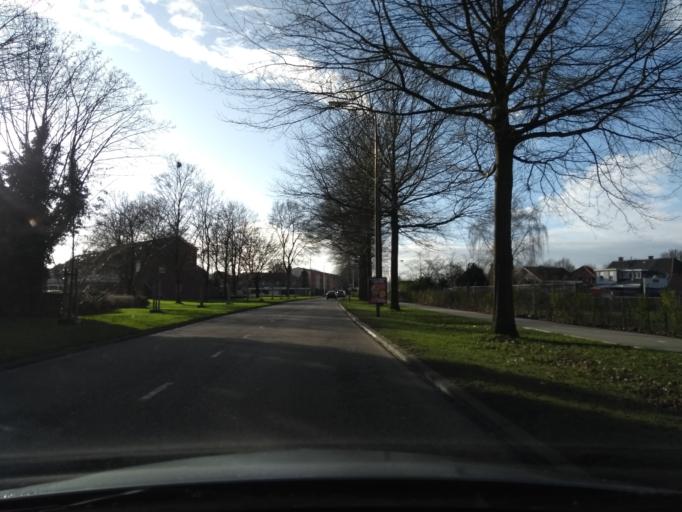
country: NL
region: Overijssel
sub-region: Gemeente Almelo
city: Almelo
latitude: 52.3712
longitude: 6.6825
